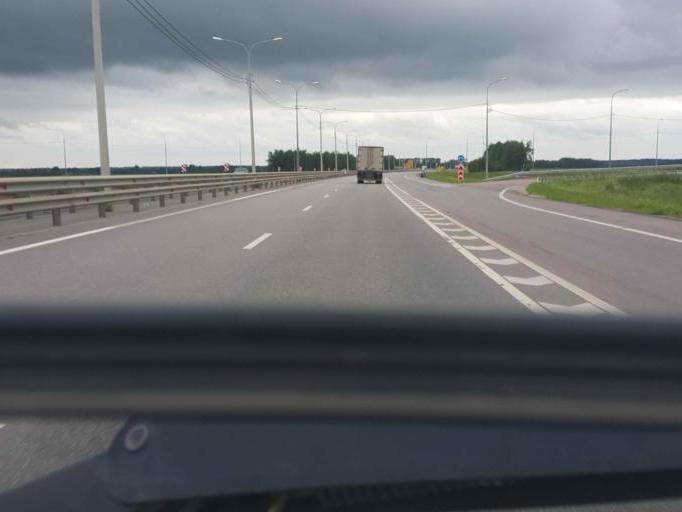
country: RU
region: Tambov
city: Zavoronezhskoye
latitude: 52.8544
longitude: 40.7827
